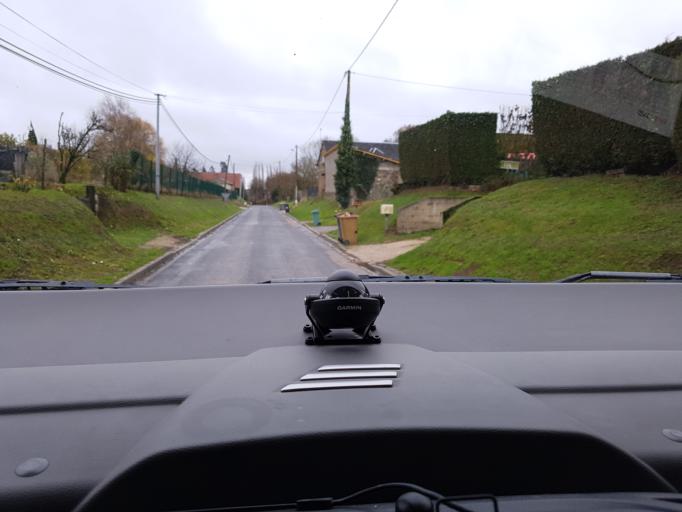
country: FR
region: Haute-Normandie
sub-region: Departement de l'Eure
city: Fleury-sur-Andelle
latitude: 49.2989
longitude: 1.3523
